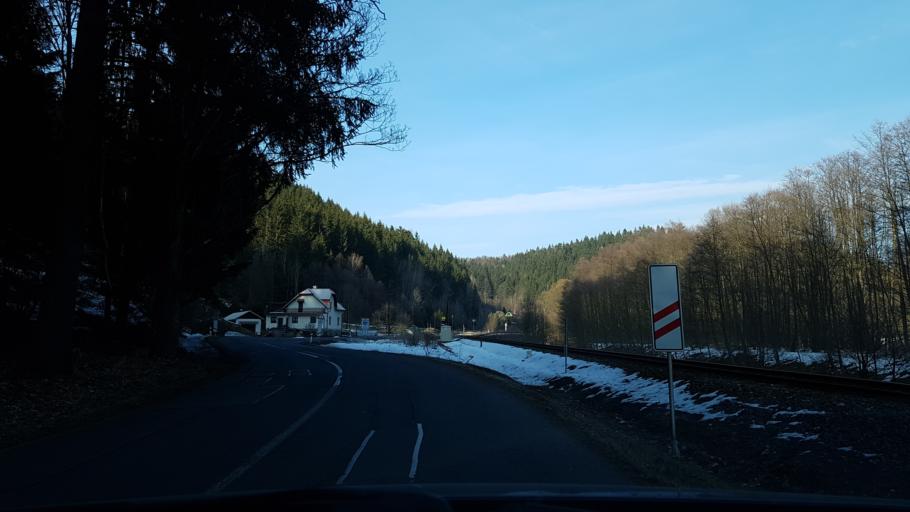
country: CZ
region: Olomoucky
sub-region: Okres Sumperk
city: Hanusovice
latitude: 50.0901
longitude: 16.9753
